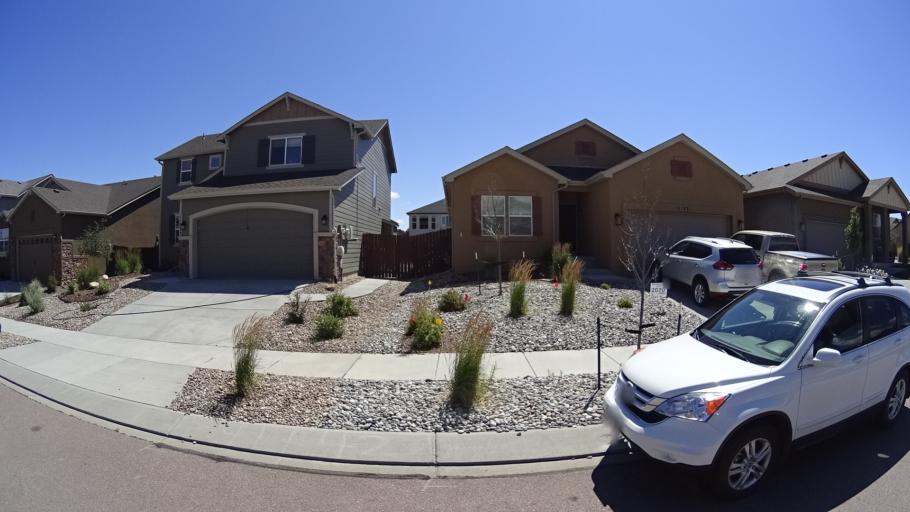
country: US
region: Colorado
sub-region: El Paso County
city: Black Forest
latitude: 38.9904
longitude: -104.7597
